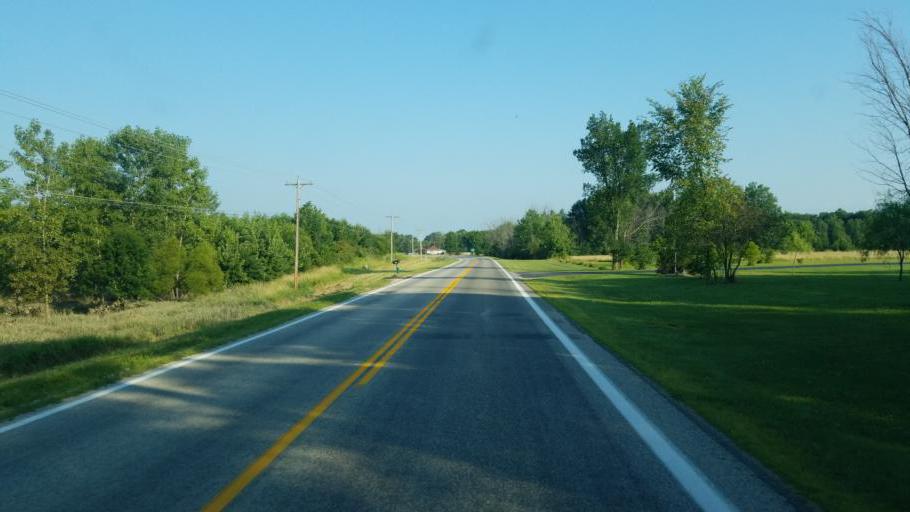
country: US
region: Ohio
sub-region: Union County
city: Richwood
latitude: 40.5742
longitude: -83.3345
